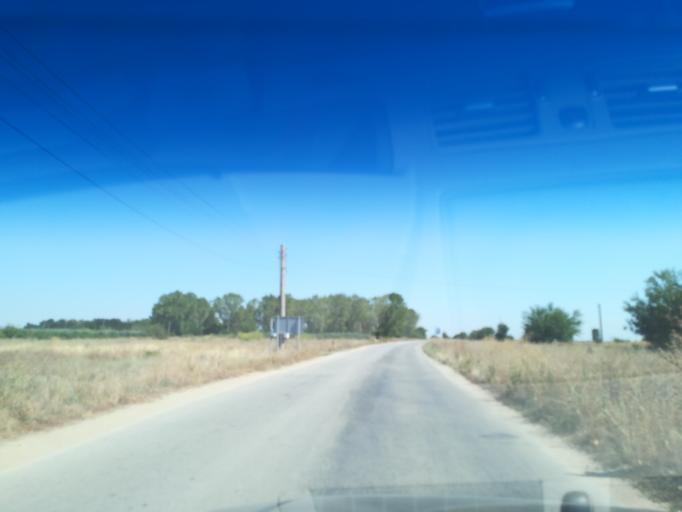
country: BG
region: Plovdiv
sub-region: Obshtina Suedinenie
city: Suedinenie
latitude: 42.2521
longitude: 24.4433
